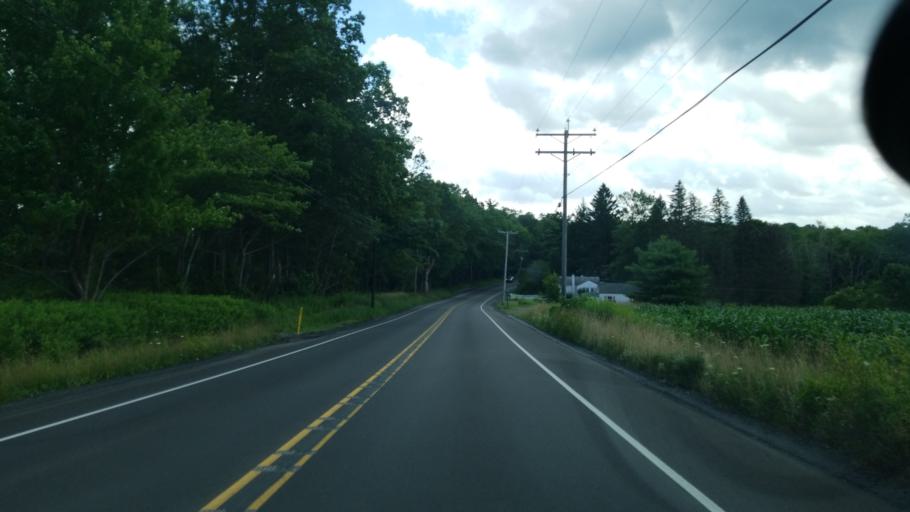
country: US
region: Pennsylvania
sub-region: Jefferson County
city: Brookville
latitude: 41.2606
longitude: -79.1075
